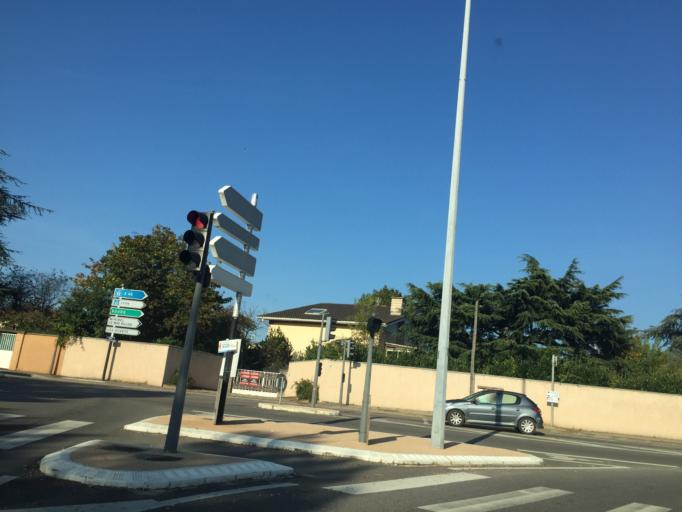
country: FR
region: Rhone-Alpes
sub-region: Departement du Rhone
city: Rillieux-la-Pape
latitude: 45.8232
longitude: 4.9074
